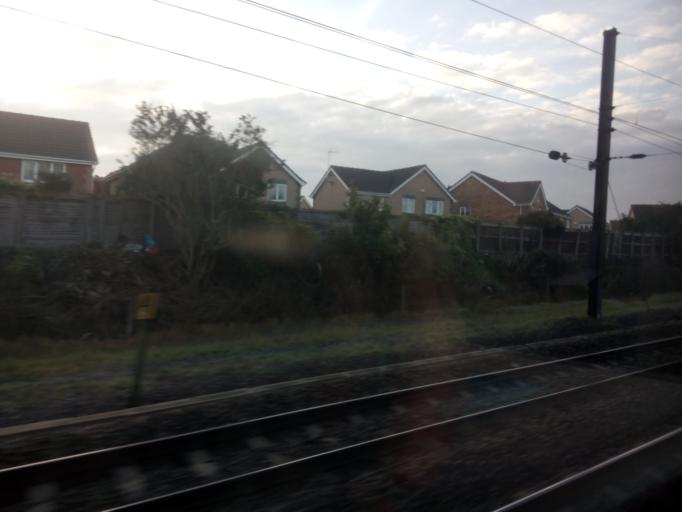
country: GB
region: England
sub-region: City of York
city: Bishopthorpe
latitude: 53.9437
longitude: -1.1103
